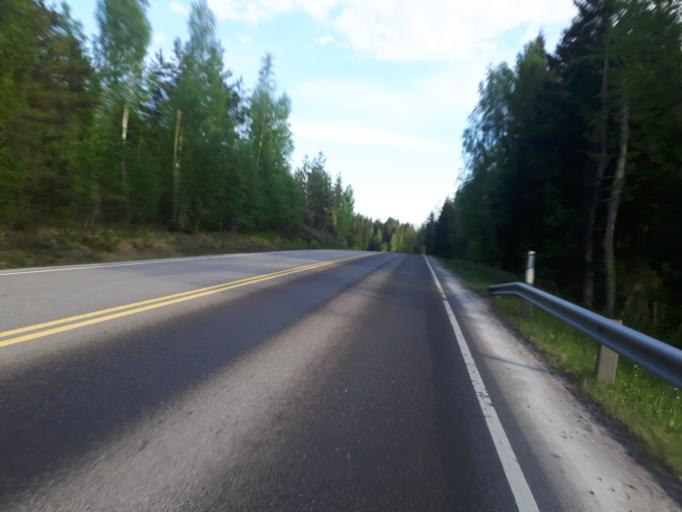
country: FI
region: Uusimaa
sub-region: Loviisa
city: Perna
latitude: 60.4676
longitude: 26.0302
